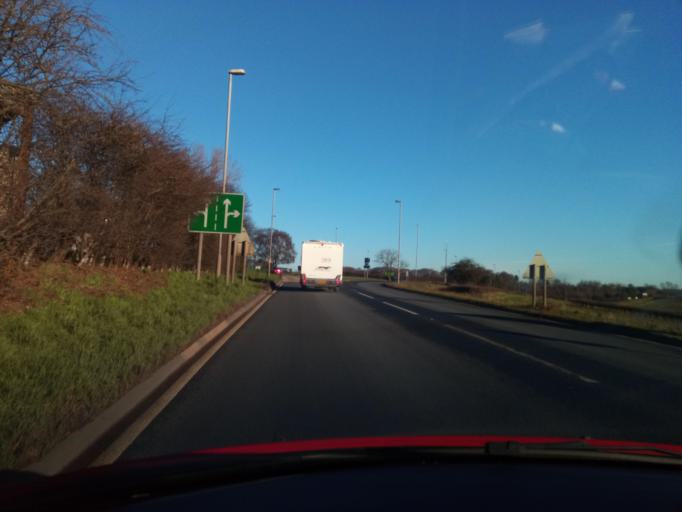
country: GB
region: England
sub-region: Nottinghamshire
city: Farnsfield
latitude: 53.1191
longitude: -1.0634
